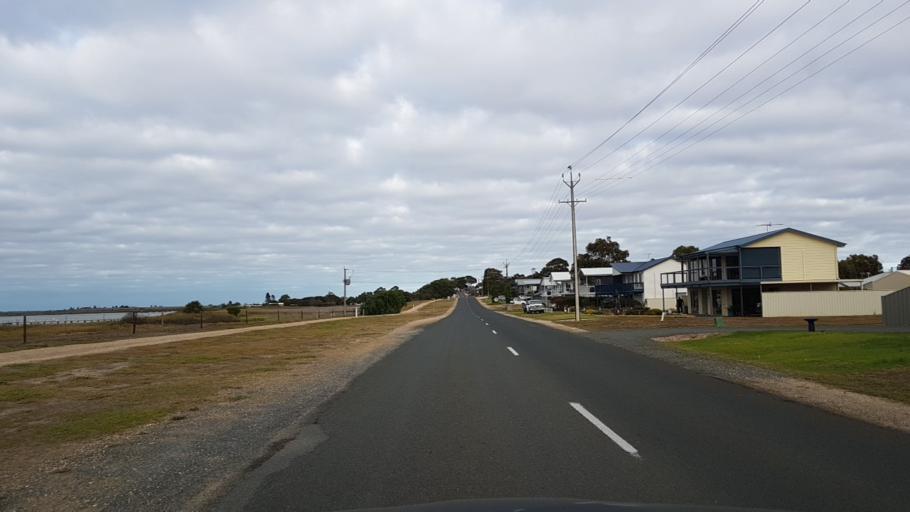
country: AU
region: South Australia
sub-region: Alexandrina
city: Langhorne Creek
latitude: -35.4021
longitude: 138.9818
